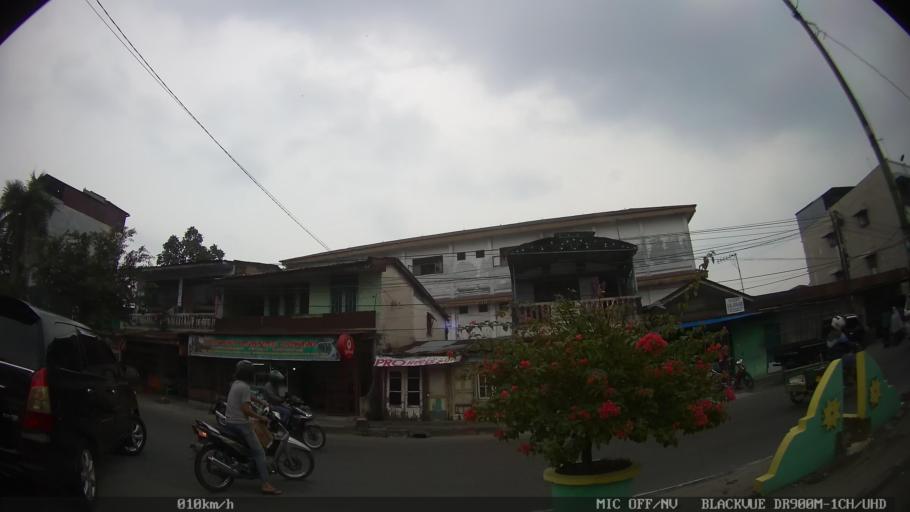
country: ID
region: North Sumatra
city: Medan
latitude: 3.5662
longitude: 98.6886
